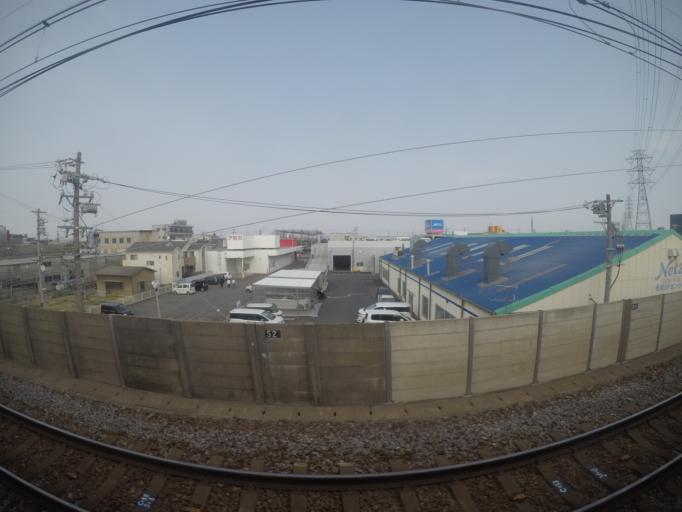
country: JP
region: Aichi
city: Obu
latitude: 35.0646
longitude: 136.9099
